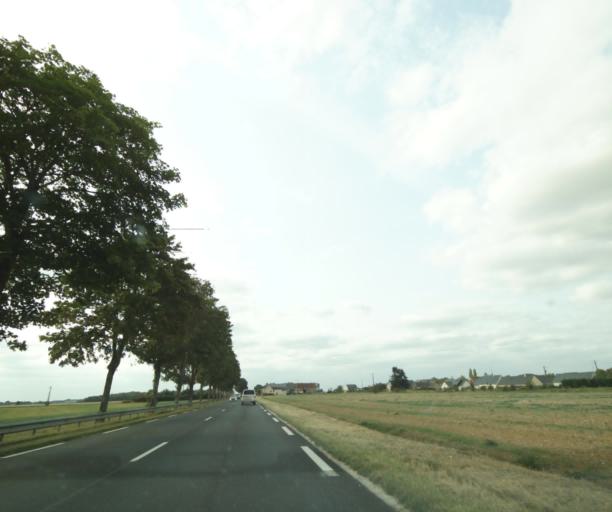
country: FR
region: Centre
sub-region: Departement d'Indre-et-Loire
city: Tauxigny
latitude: 47.2352
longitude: 0.8697
